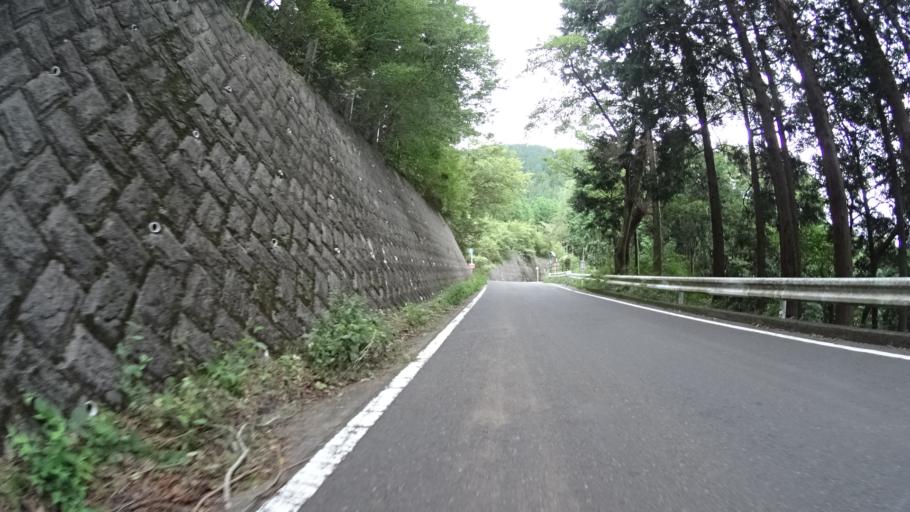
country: JP
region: Kanagawa
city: Hadano
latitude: 35.4196
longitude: 139.2140
